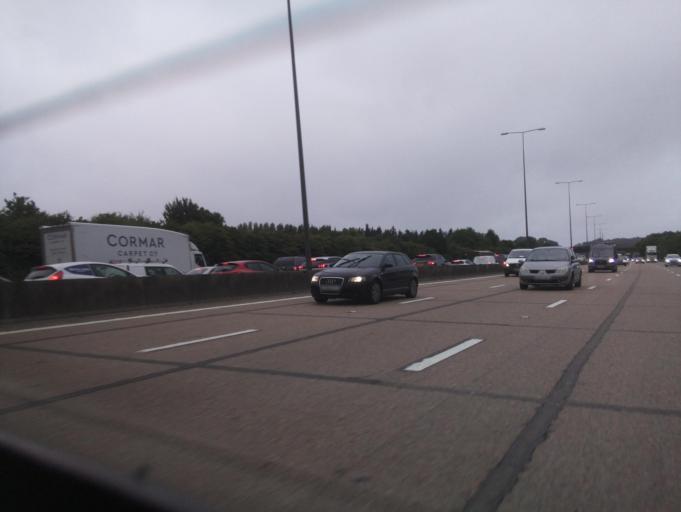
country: GB
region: England
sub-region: Surrey
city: Great Bookham
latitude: 51.3125
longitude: -0.3729
